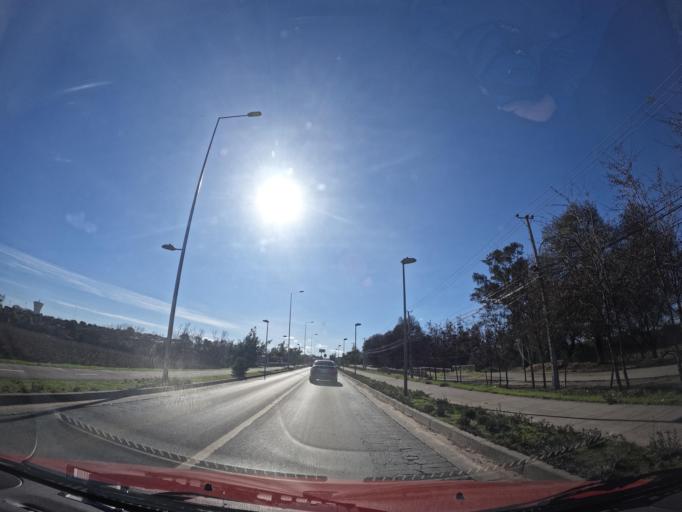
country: CL
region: Maule
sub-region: Provincia de Cauquenes
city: Cauquenes
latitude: -35.9760
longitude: -72.3153
